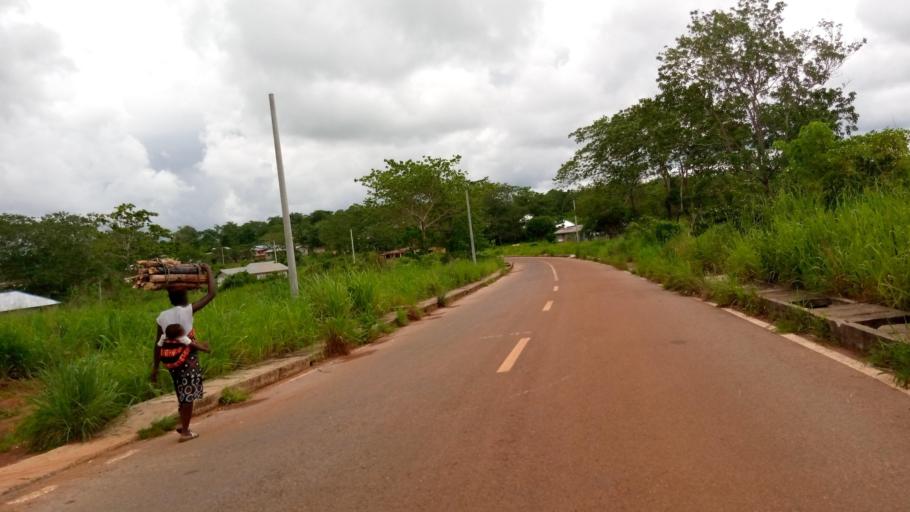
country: SL
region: Southern Province
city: Moyamba
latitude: 8.1621
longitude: -12.4503
